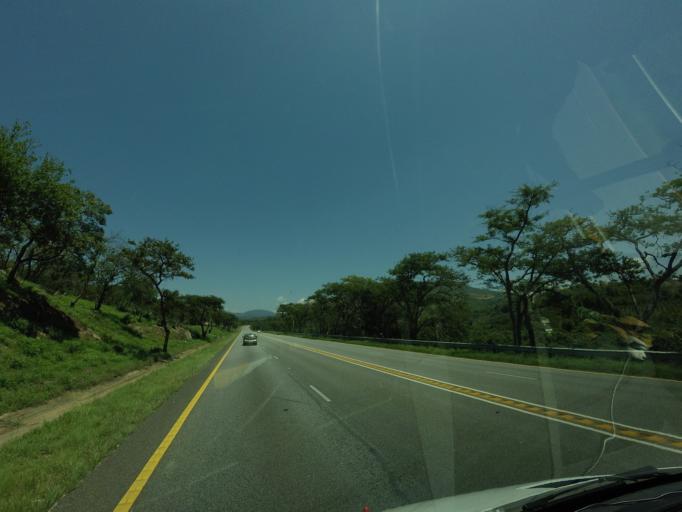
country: ZA
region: Mpumalanga
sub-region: Ehlanzeni District
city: Nelspruit
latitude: -25.4277
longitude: 30.7828
